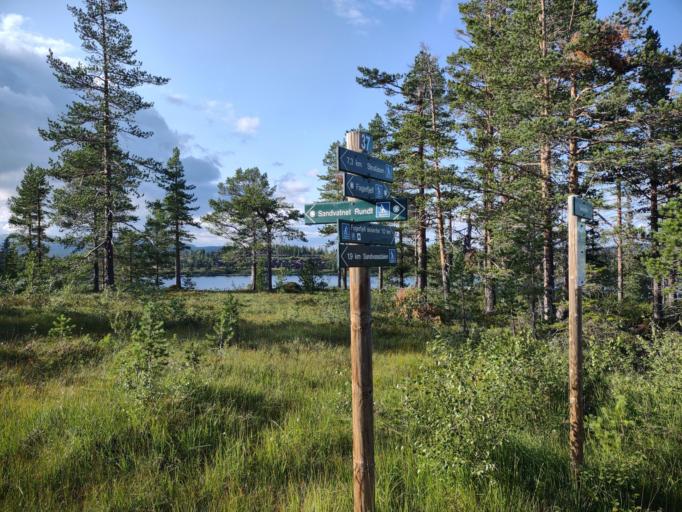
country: NO
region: Buskerud
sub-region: Rollag
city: Rollag
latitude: 59.8274
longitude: 9.3210
